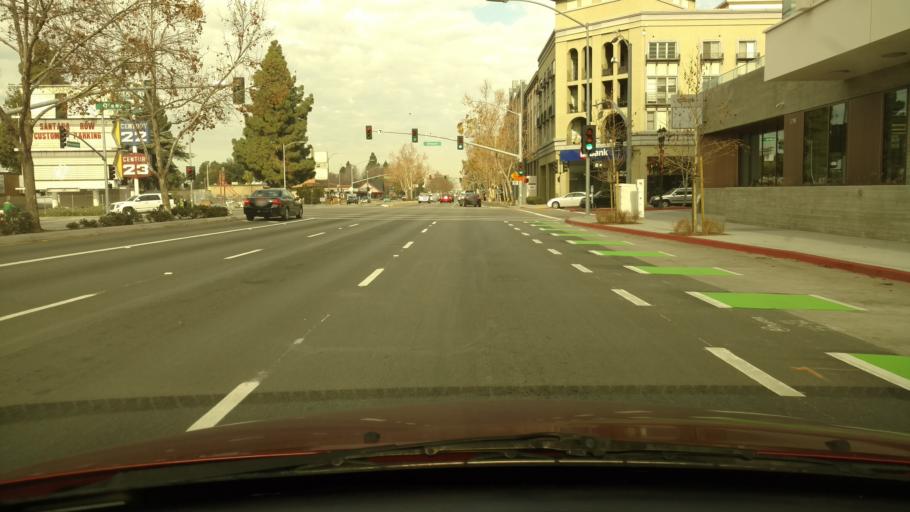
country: US
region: California
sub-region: Santa Clara County
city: Burbank
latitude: 37.3186
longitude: -121.9500
